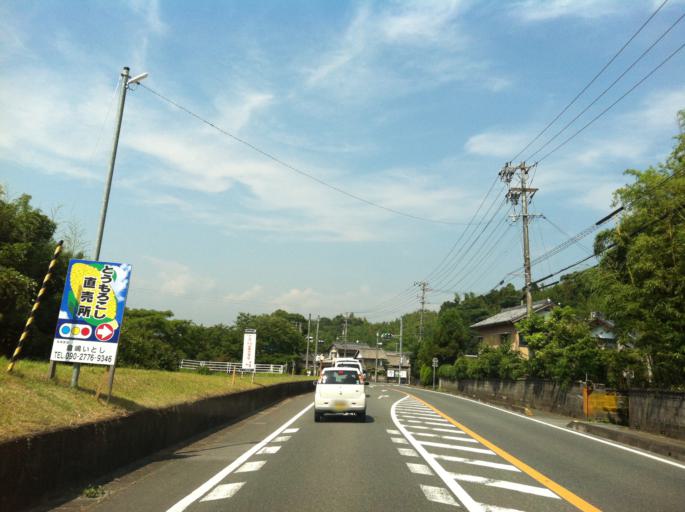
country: JP
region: Shizuoka
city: Mori
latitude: 34.8014
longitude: 137.9165
